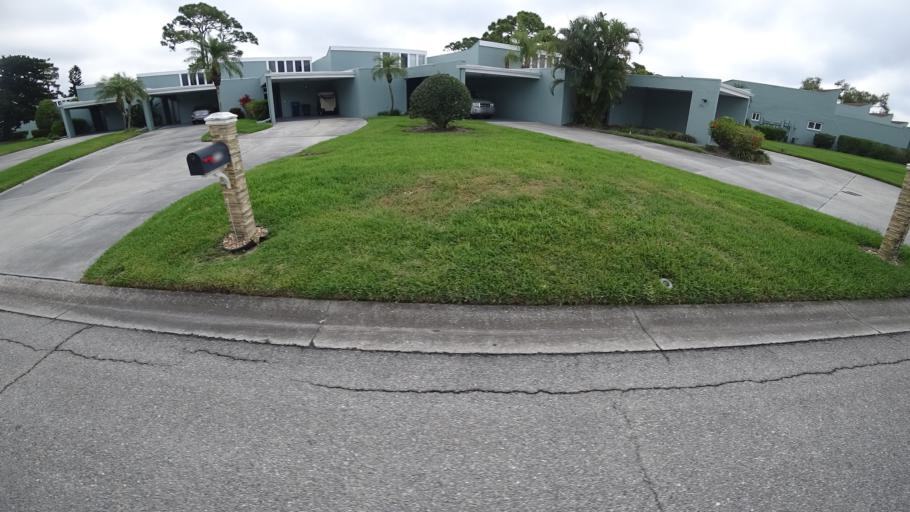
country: US
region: Florida
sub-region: Manatee County
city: Bayshore Gardens
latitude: 27.4341
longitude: -82.6021
